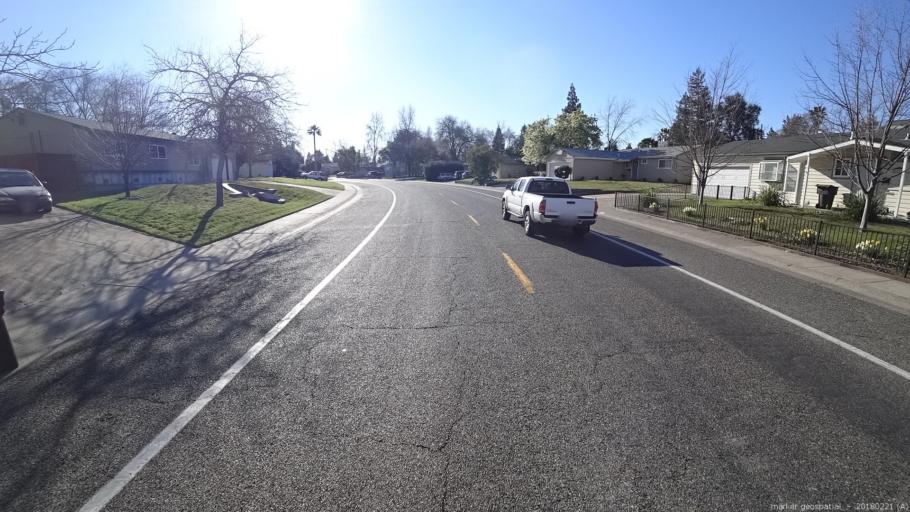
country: US
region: California
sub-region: Sacramento County
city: Orangevale
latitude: 38.6867
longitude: -121.2464
